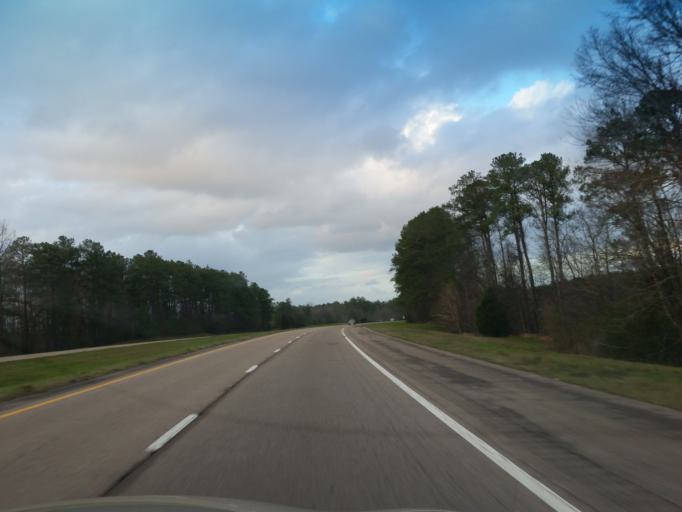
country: US
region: Mississippi
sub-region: Clarke County
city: Stonewall
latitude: 32.0416
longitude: -88.9206
